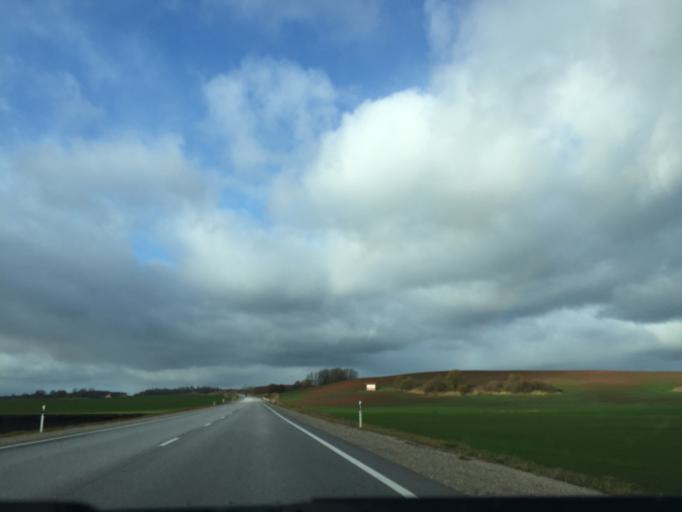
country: LV
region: Tukuma Rajons
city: Tukums
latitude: 56.9679
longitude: 23.0642
